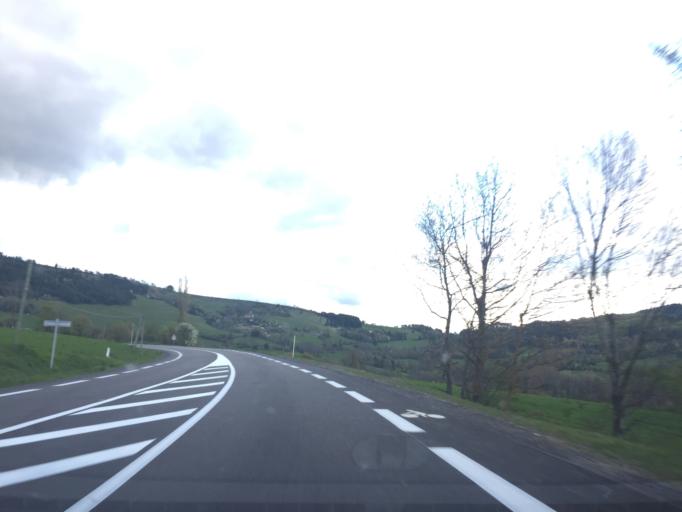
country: FR
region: Rhone-Alpes
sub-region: Departement de l'Isere
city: La Motte-Saint-Martin
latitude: 44.8921
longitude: 5.6180
